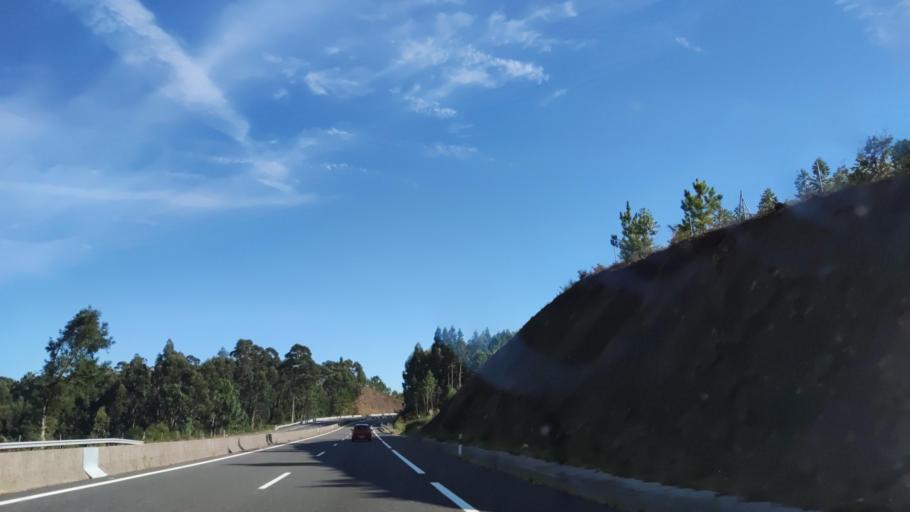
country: ES
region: Galicia
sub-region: Provincia da Coruna
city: Boiro
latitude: 42.5977
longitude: -8.9692
